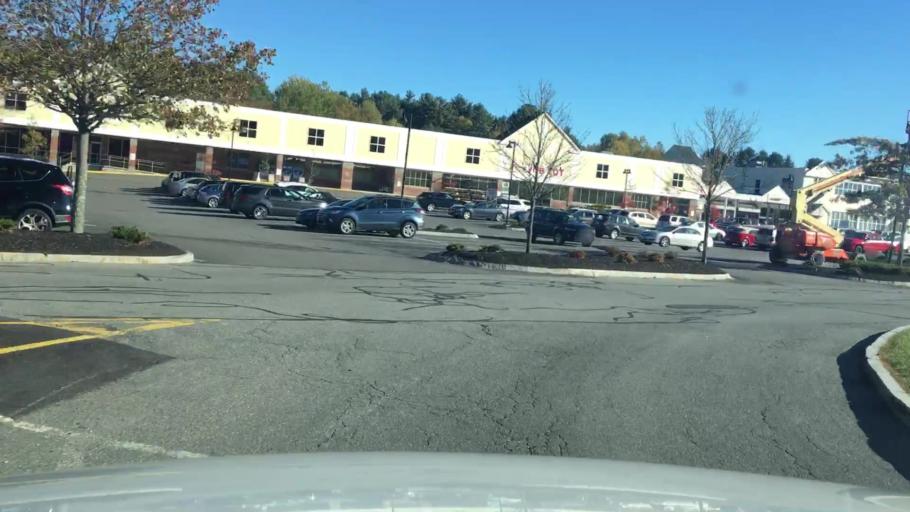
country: US
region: Maine
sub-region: Cumberland County
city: Falmouth
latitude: 43.7257
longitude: -70.2309
